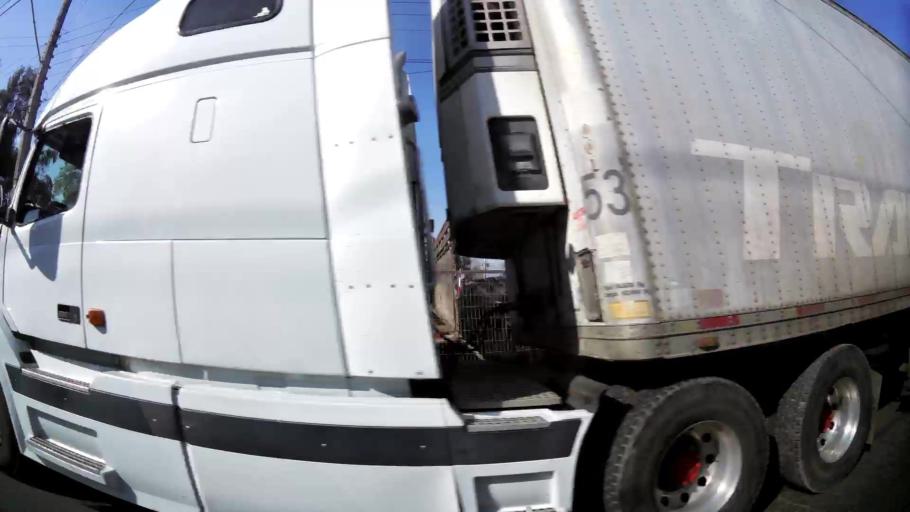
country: CL
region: Santiago Metropolitan
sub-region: Provincia de Santiago
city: Lo Prado
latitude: -33.4144
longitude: -70.7589
